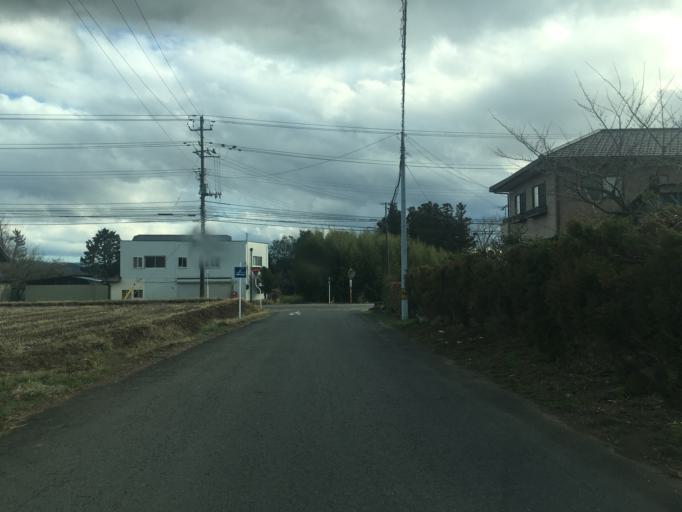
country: JP
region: Fukushima
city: Yanagawamachi-saiwaicho
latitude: 37.8756
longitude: 140.5739
